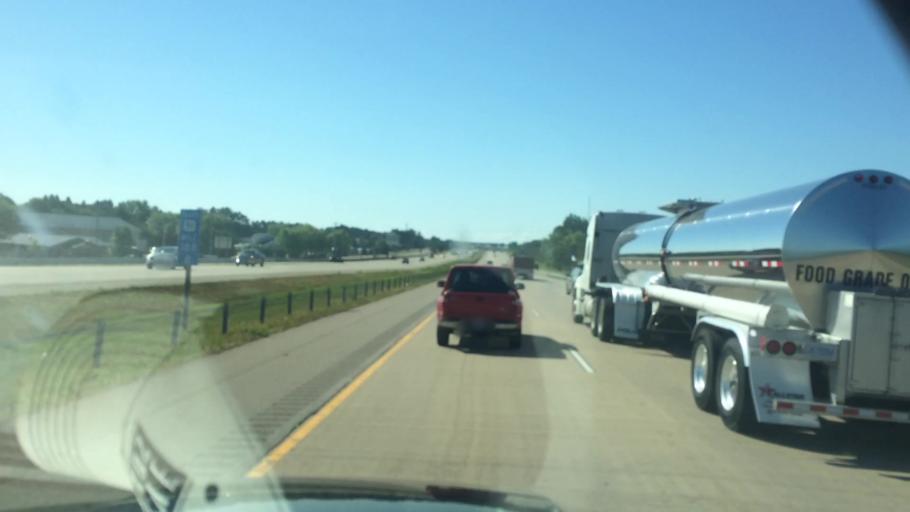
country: US
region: Wisconsin
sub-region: Marathon County
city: Rib Mountain
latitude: 44.9108
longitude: -89.6504
